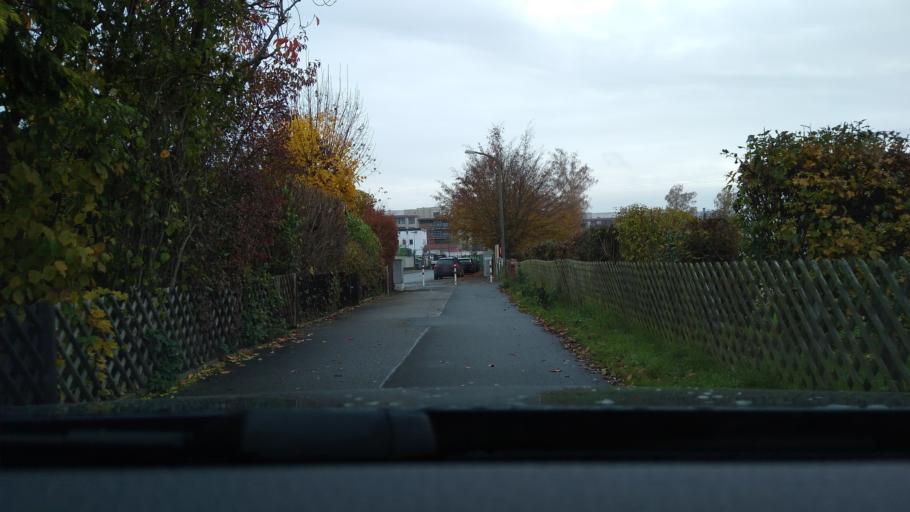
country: DE
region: Bavaria
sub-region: Regierungsbezirk Mittelfranken
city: Wetzendorf
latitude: 49.5176
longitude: 11.0302
